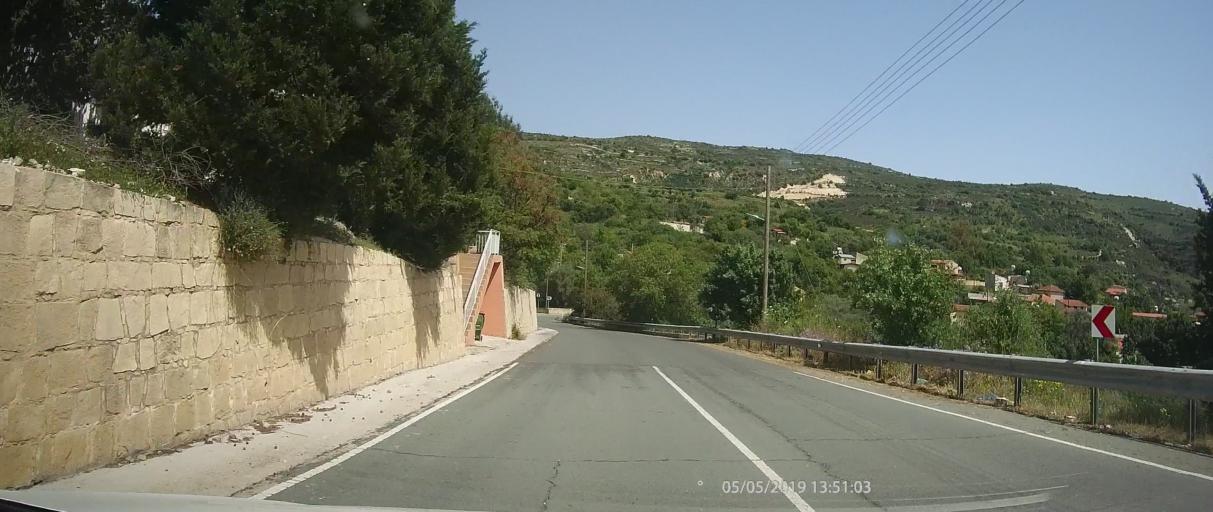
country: CY
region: Limassol
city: Pachna
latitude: 34.8383
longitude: 32.7356
